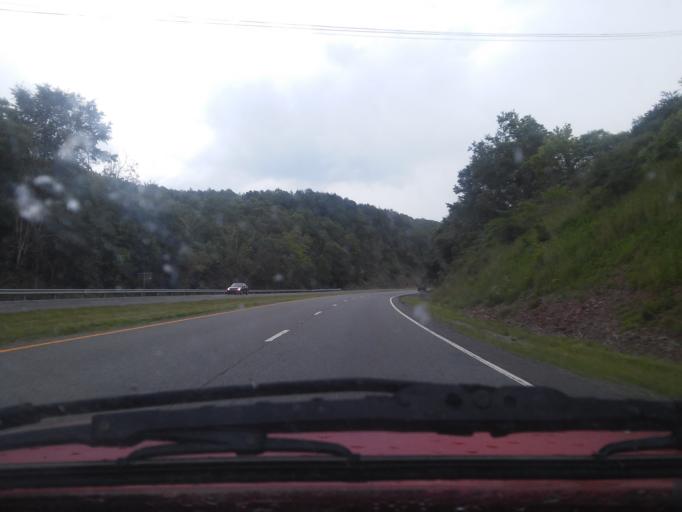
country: US
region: Virginia
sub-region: Montgomery County
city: Prices Fork
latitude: 37.3069
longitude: -80.5148
